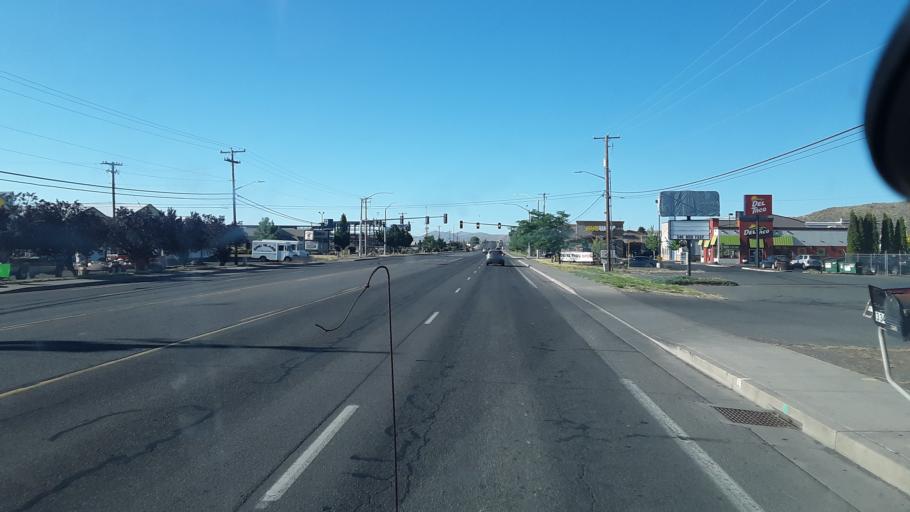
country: US
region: Oregon
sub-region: Klamath County
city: Altamont
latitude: 42.1970
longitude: -121.7573
